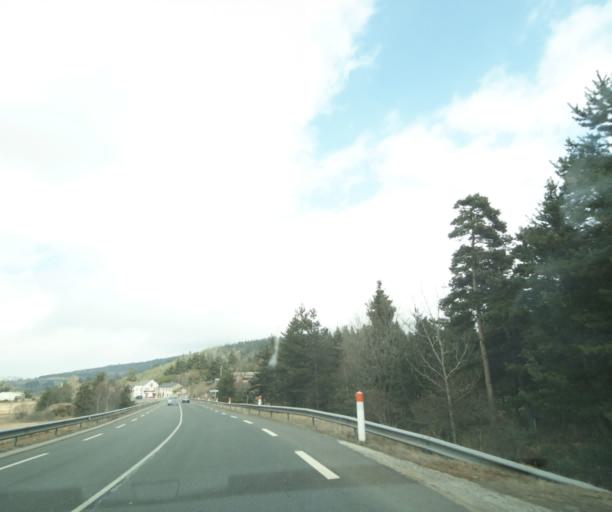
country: FR
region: Languedoc-Roussillon
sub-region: Departement de la Lozere
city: Mende
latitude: 44.6026
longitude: 3.6740
